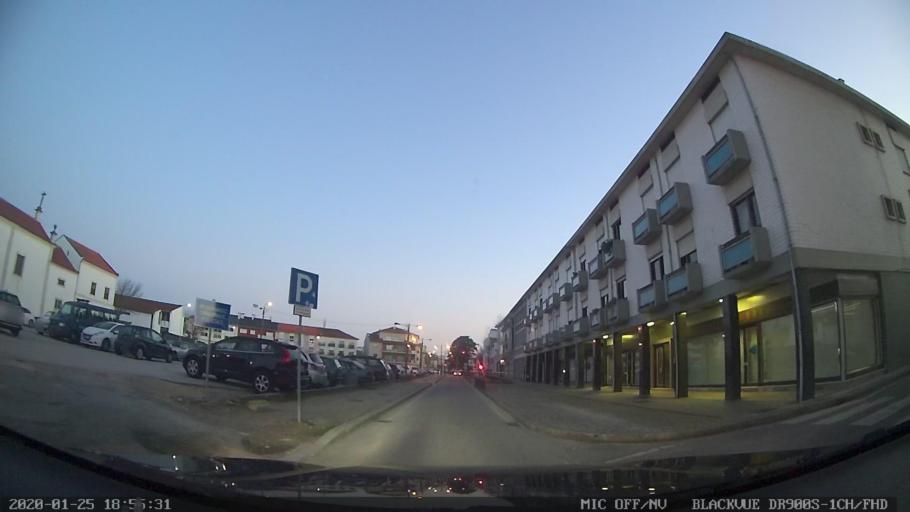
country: PT
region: Aveiro
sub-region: Aveiro
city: Aveiro
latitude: 40.6382
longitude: -8.6540
